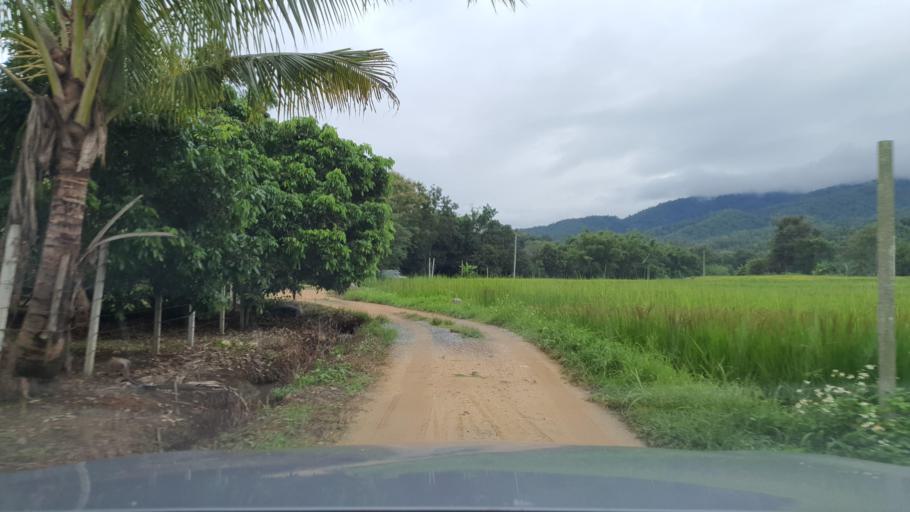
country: TH
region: Chiang Mai
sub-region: Amphoe Chiang Dao
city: Chiang Dao
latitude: 19.3311
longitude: 98.9352
